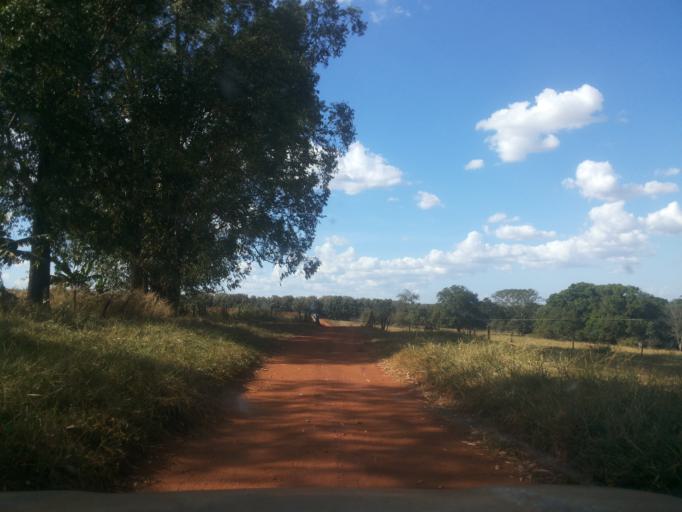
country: BR
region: Minas Gerais
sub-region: Capinopolis
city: Capinopolis
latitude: -18.5796
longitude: -49.4908
